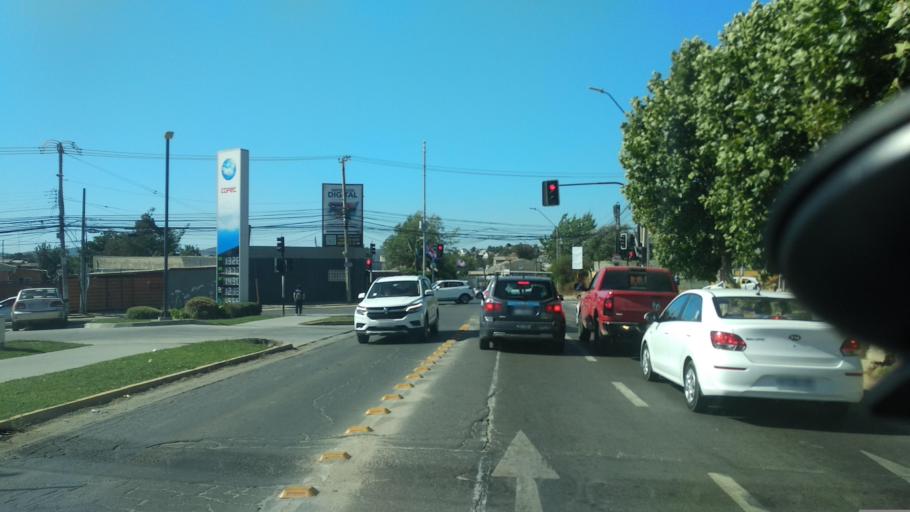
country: CL
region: Valparaiso
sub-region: Provincia de Marga Marga
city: Villa Alemana
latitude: -33.0592
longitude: -71.3725
